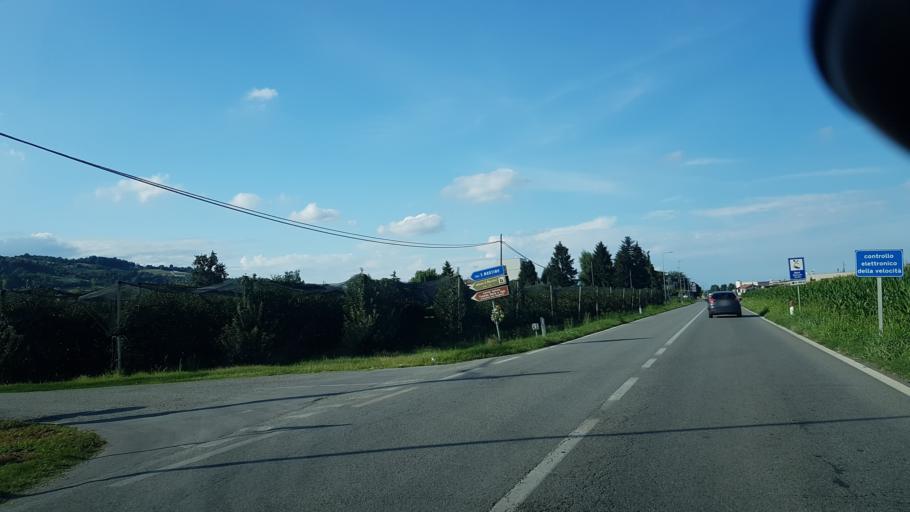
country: IT
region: Piedmont
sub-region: Provincia di Cuneo
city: Costiglione Saluzzo
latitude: 44.5403
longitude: 7.4877
